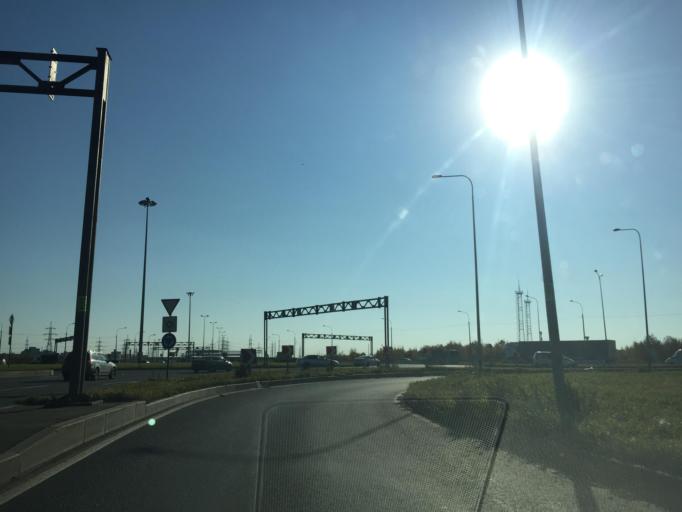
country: RU
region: St.-Petersburg
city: Metallostroy
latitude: 59.7492
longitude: 30.5299
